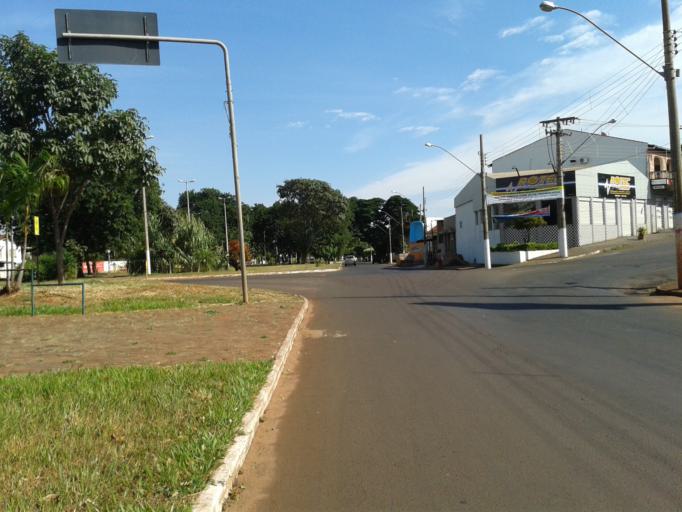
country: BR
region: Minas Gerais
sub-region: Ituiutaba
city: Ituiutaba
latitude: -18.9718
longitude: -49.4552
